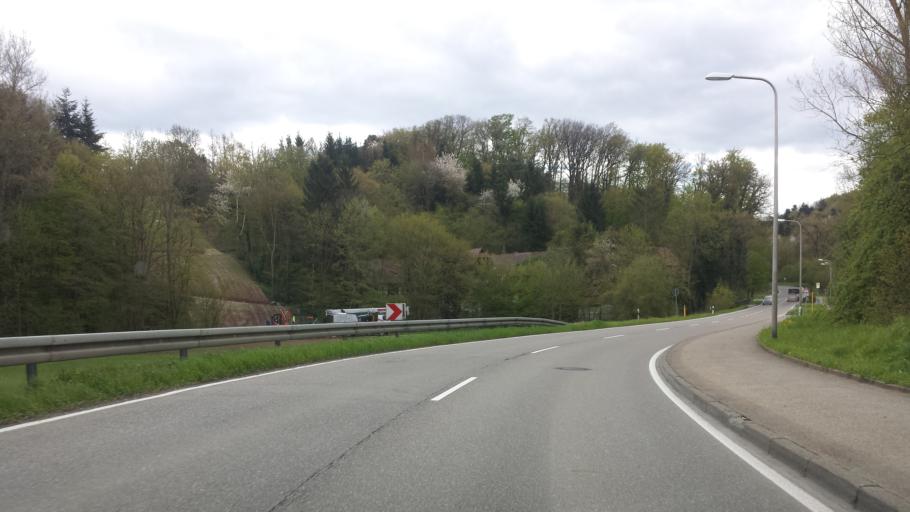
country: DE
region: Baden-Wuerttemberg
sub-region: Karlsruhe Region
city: Niefern-Oschelbronn
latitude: 48.9063
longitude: 8.7910
